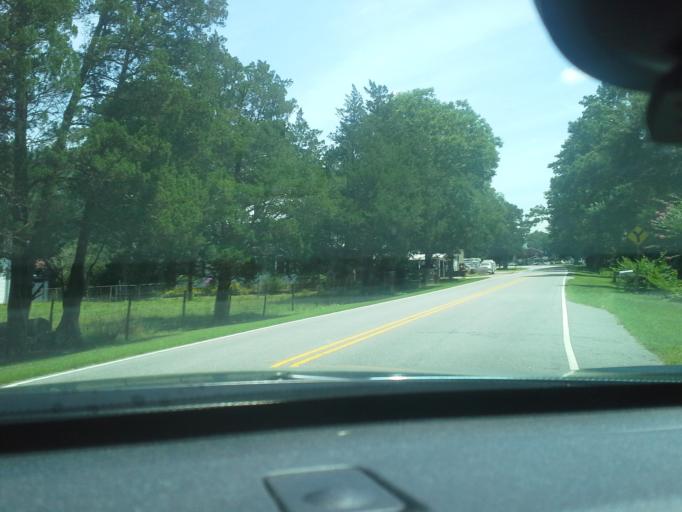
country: US
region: North Carolina
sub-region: Washington County
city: Plymouth
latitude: 35.9043
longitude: -76.6765
